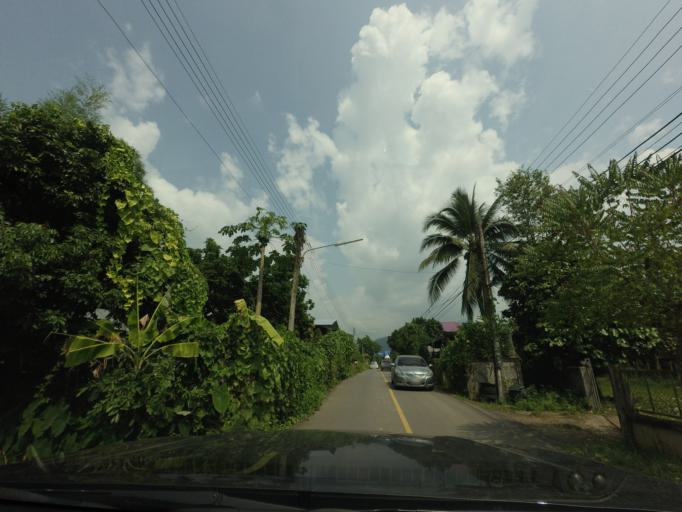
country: TH
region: Nan
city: Pua
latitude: 19.1672
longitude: 100.9358
